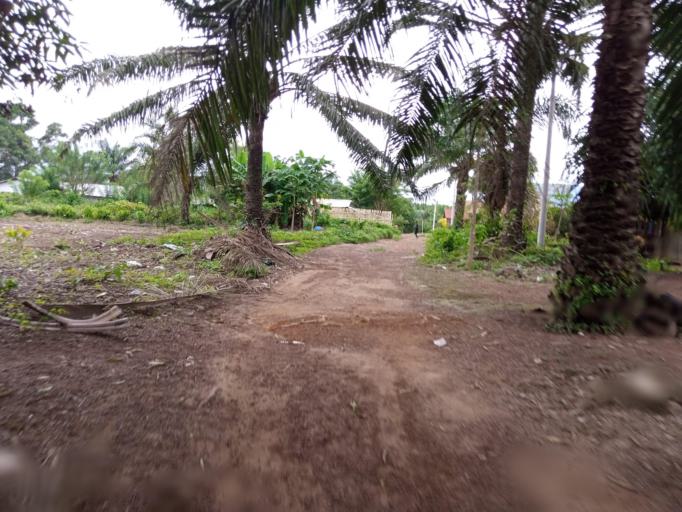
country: SL
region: Southern Province
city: Moyamba
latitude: 8.1674
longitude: -12.4270
